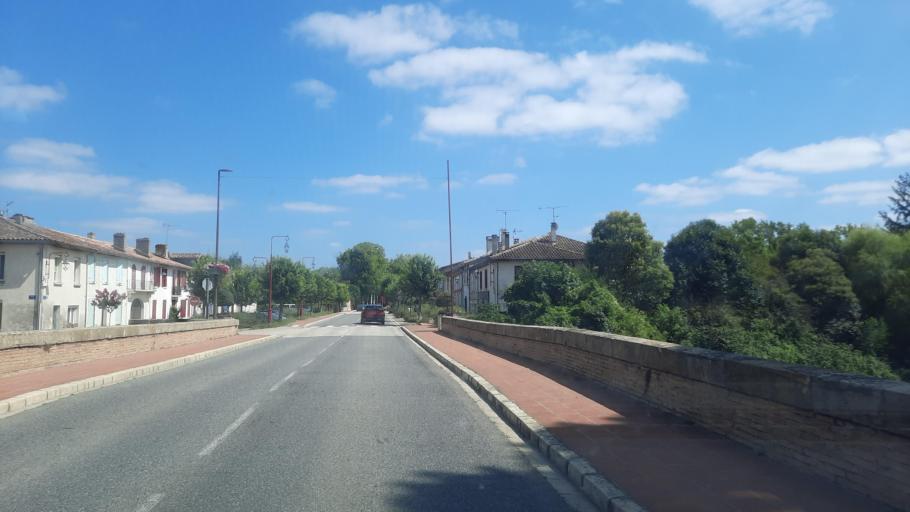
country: FR
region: Midi-Pyrenees
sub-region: Departement du Gers
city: Lombez
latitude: 43.4754
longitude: 0.9124
